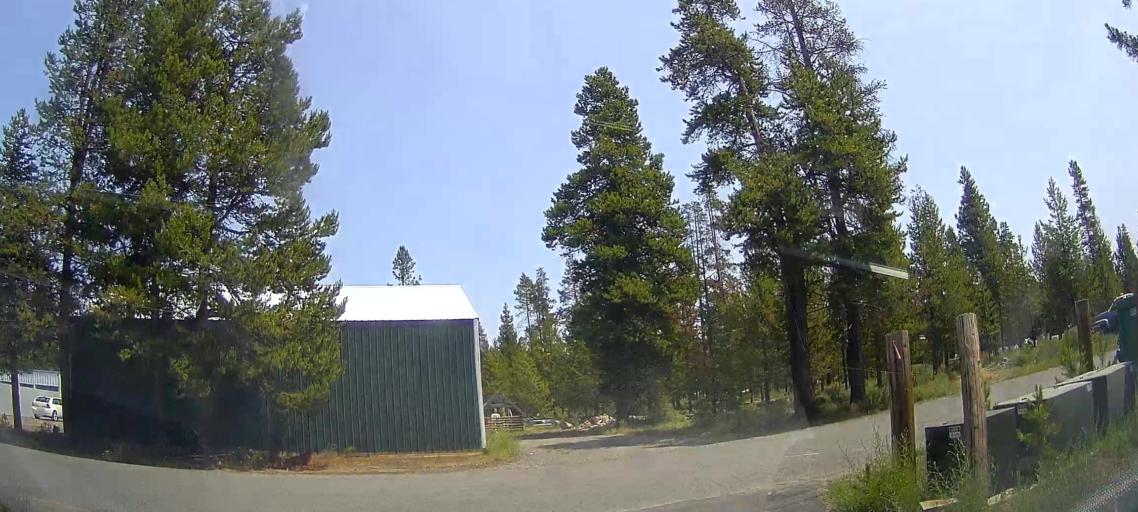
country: US
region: Oregon
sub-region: Deschutes County
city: La Pine
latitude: 43.7110
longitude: -121.4738
